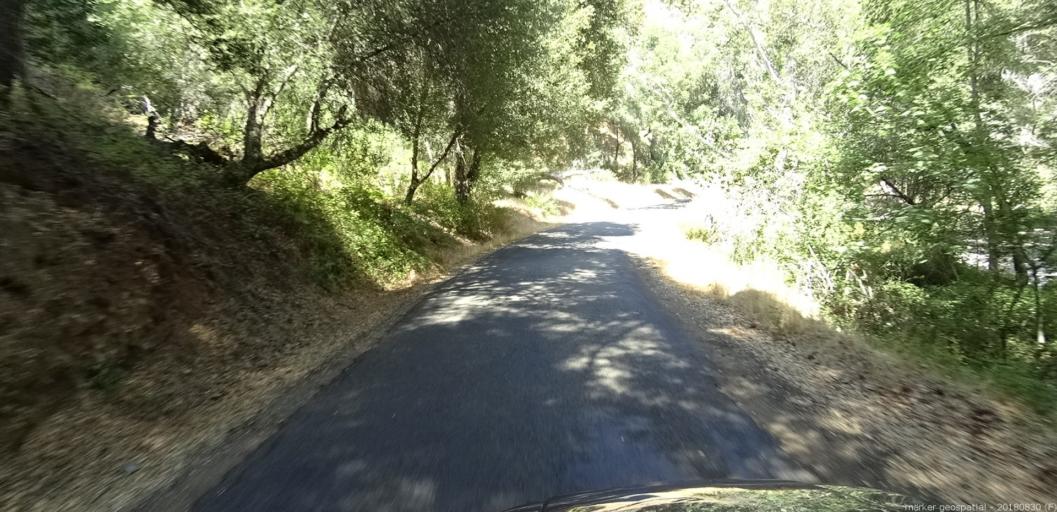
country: US
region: California
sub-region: Monterey County
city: Greenfield
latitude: 36.0155
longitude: -121.4189
